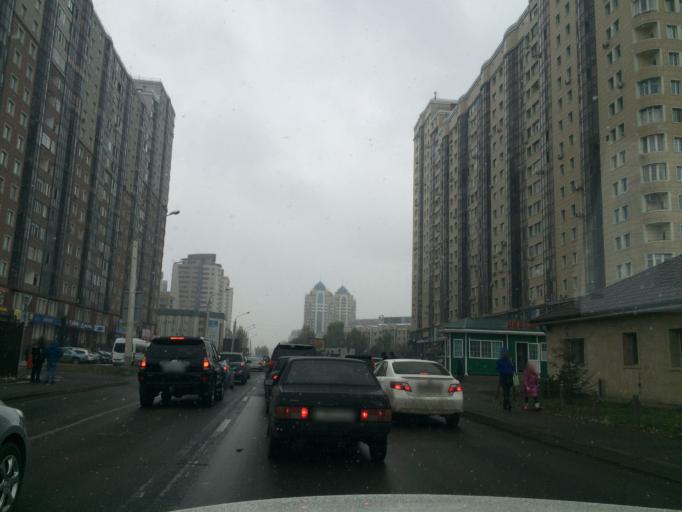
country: KZ
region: Astana Qalasy
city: Astana
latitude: 51.1673
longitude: 71.4429
